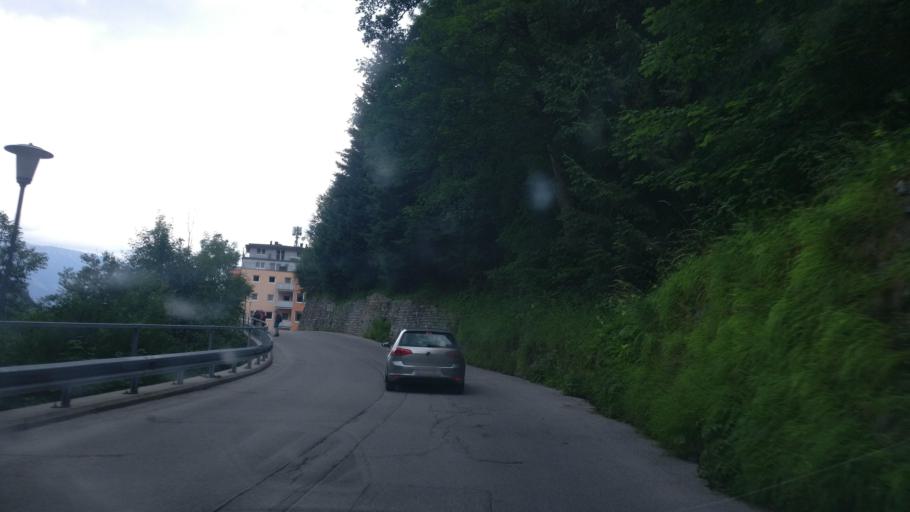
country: AT
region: Salzburg
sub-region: Politischer Bezirk Sankt Johann im Pongau
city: Bad Gastein
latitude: 47.1145
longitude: 13.1395
